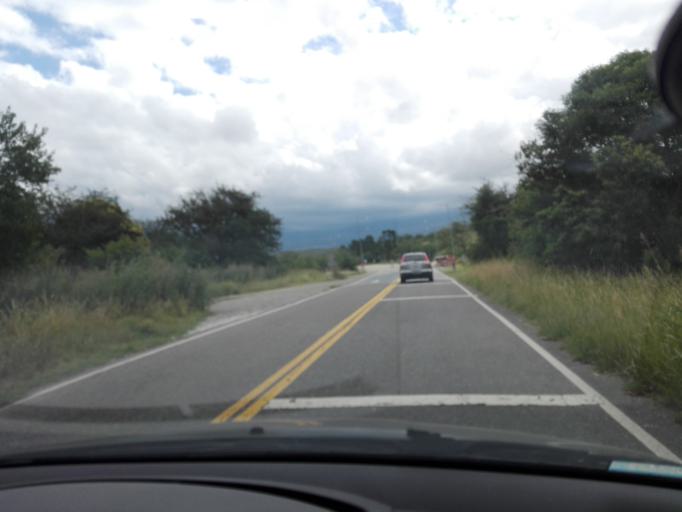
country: AR
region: Cordoba
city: Cuesta Blanca
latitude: -31.6061
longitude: -64.5588
